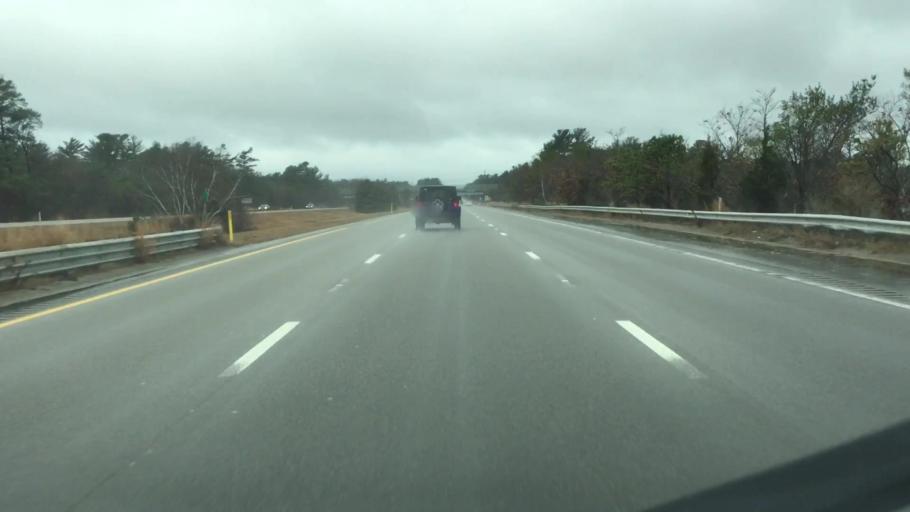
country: US
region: Massachusetts
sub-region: Plymouth County
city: Onset
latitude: 41.7663
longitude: -70.6751
